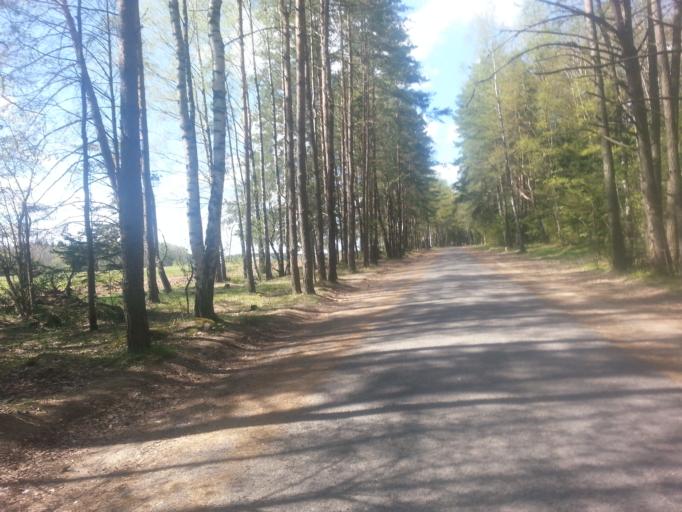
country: BY
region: Minsk
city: Narach
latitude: 54.9193
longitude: 26.6972
